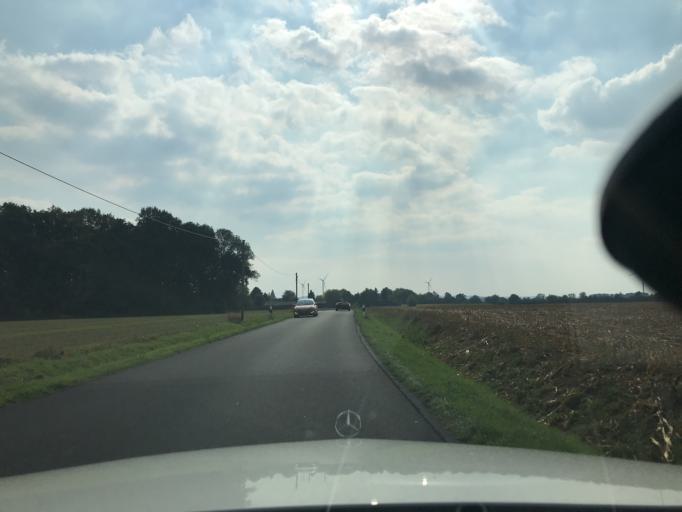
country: DE
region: North Rhine-Westphalia
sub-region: Regierungsbezirk Arnsberg
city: Werl
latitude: 51.5860
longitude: 7.8693
